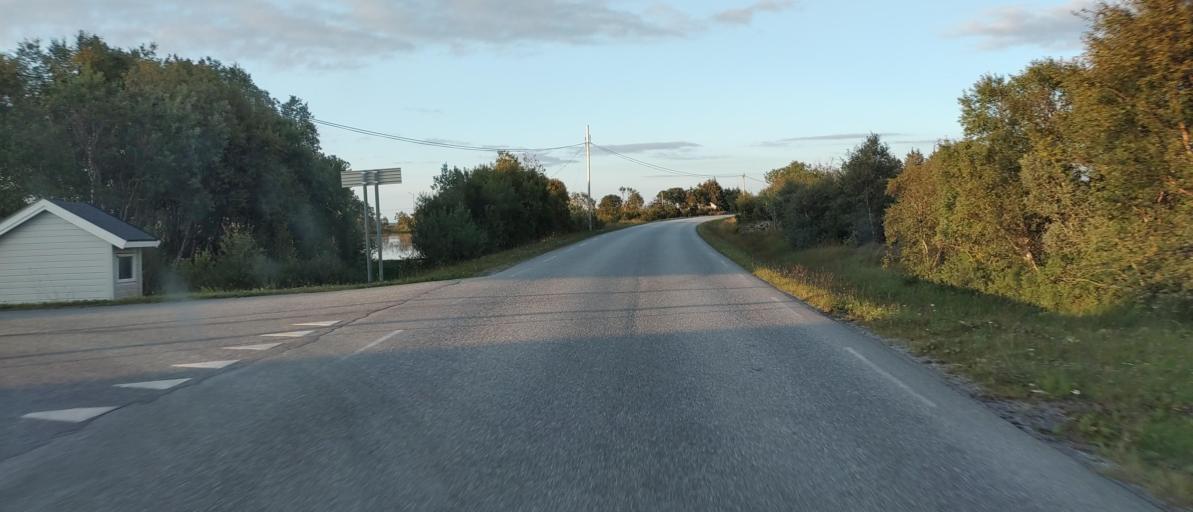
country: NO
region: More og Romsdal
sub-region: Fraena
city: Elnesvagen
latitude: 62.9890
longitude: 7.1685
